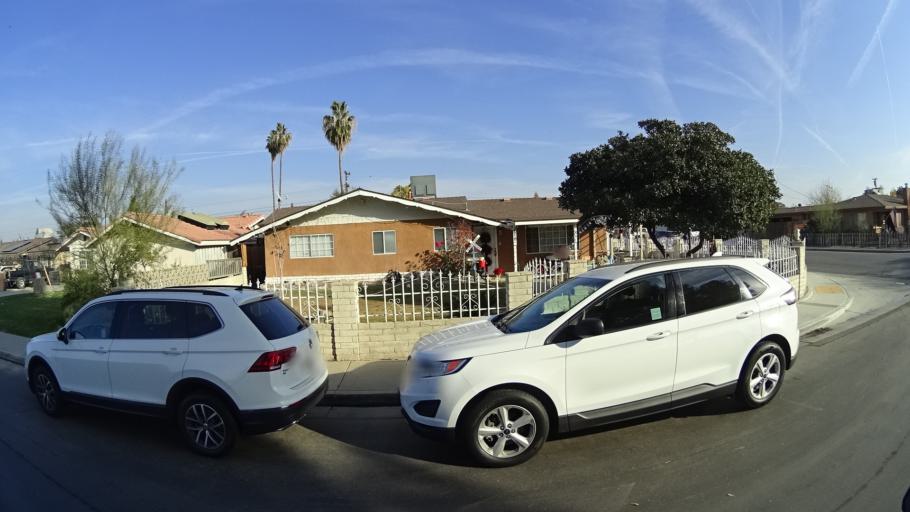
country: US
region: California
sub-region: Kern County
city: Bakersfield
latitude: 35.3215
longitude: -119.0243
